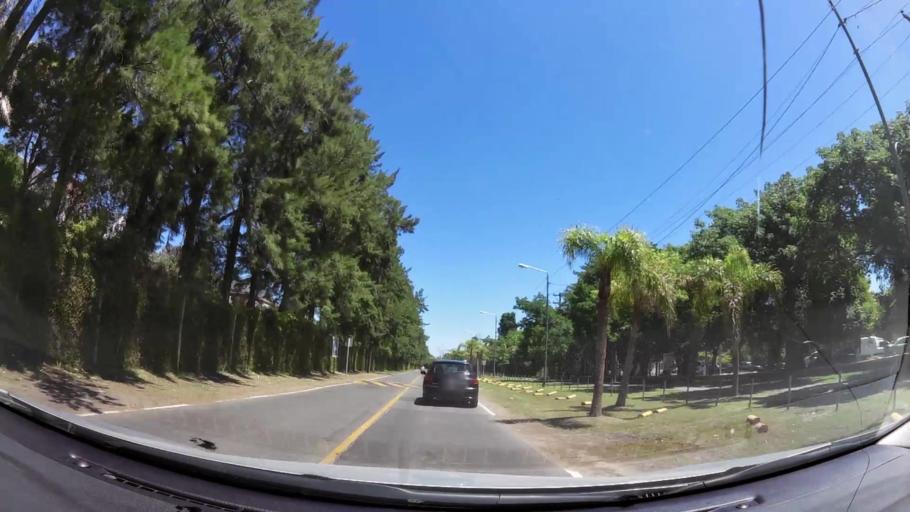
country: AR
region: Buenos Aires
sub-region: Partido de San Isidro
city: San Isidro
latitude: -34.4411
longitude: -58.5385
